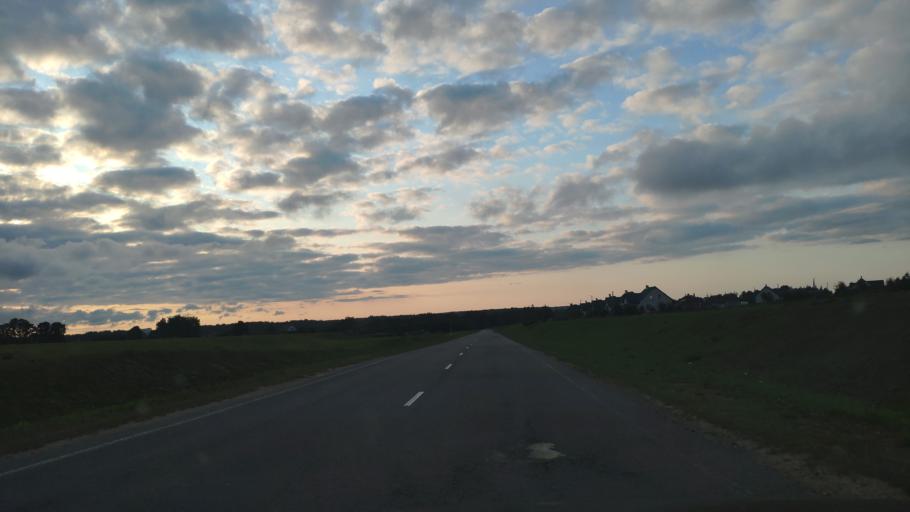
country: BY
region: Minsk
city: Azyartso
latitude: 53.8362
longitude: 27.3410
